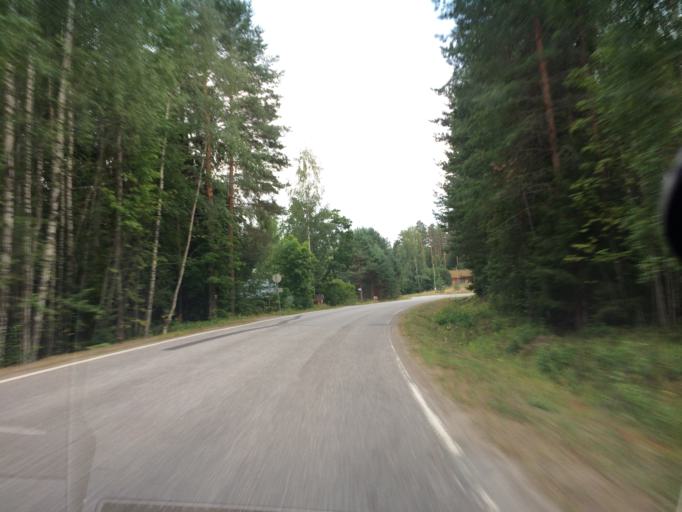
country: FI
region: Pirkanmaa
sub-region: Tampere
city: Luopioinen
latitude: 61.2483
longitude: 24.7083
